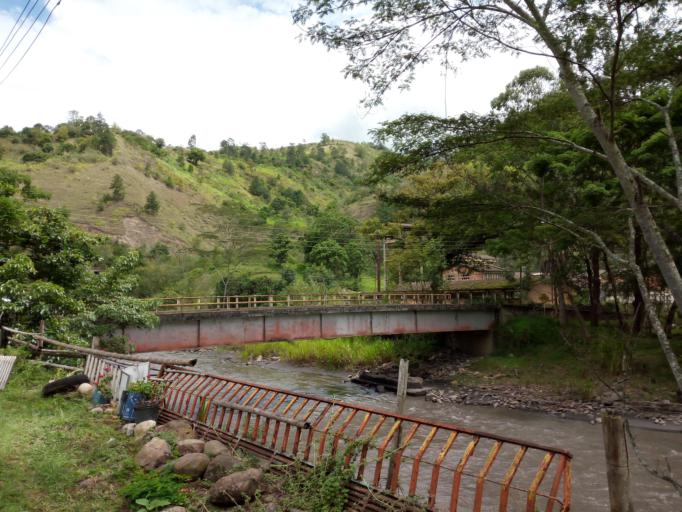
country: CO
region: Boyaca
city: Somondoco
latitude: 5.0057
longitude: -73.4310
